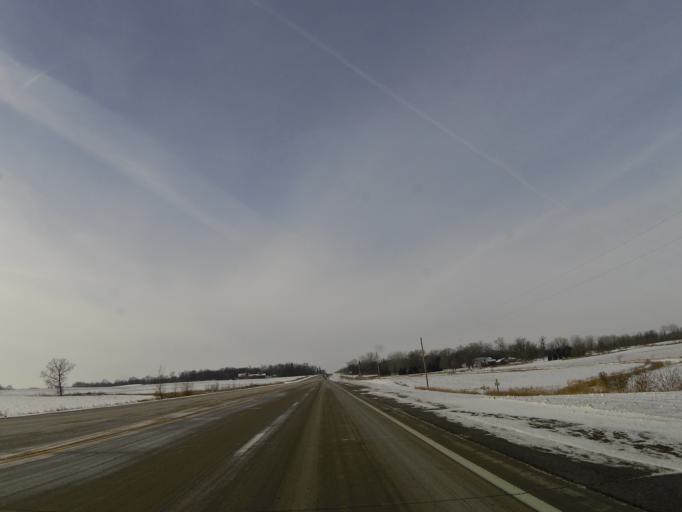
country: US
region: Minnesota
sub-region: McLeod County
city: Hutchinson
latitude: 44.8926
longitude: -94.2573
